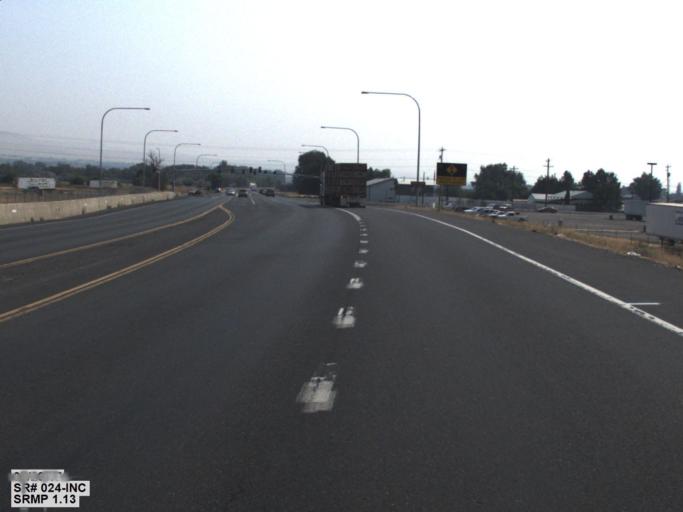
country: US
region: Washington
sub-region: Yakima County
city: Union Gap
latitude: 46.5771
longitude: -120.4545
